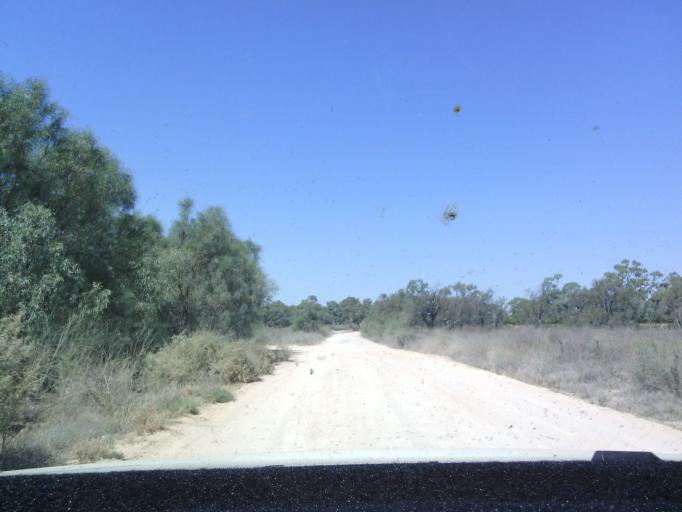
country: AU
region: South Australia
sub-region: Renmark Paringa
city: Renmark
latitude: -34.2169
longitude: 140.7384
